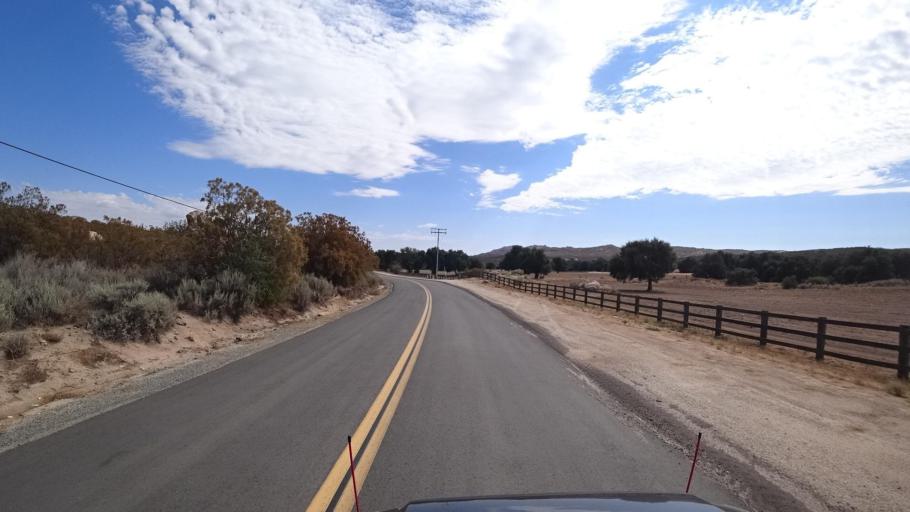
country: MX
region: Baja California
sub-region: Tecate
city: Cereso del Hongo
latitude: 32.6513
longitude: -116.2908
